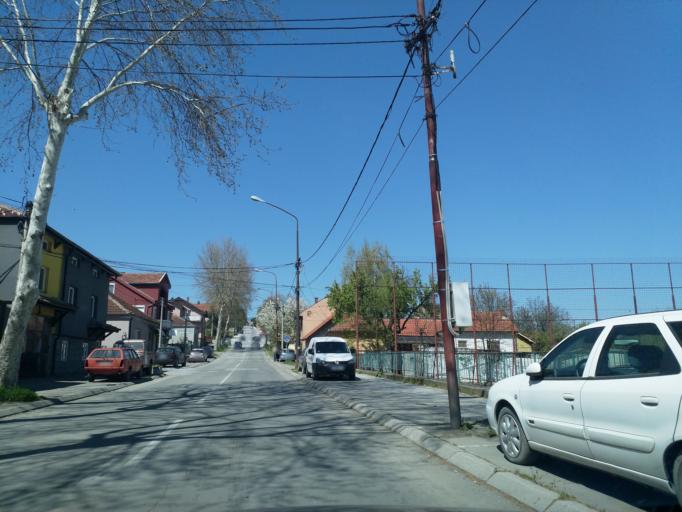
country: RS
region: Central Serbia
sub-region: Kolubarski Okrug
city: Valjevo
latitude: 44.2724
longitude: 19.8774
